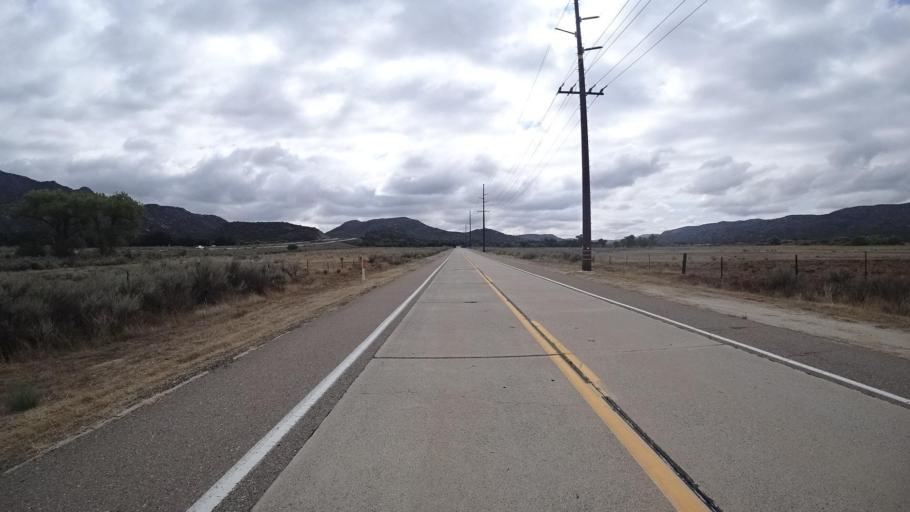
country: US
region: California
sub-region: San Diego County
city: Pine Valley
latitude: 32.7409
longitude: -116.4816
